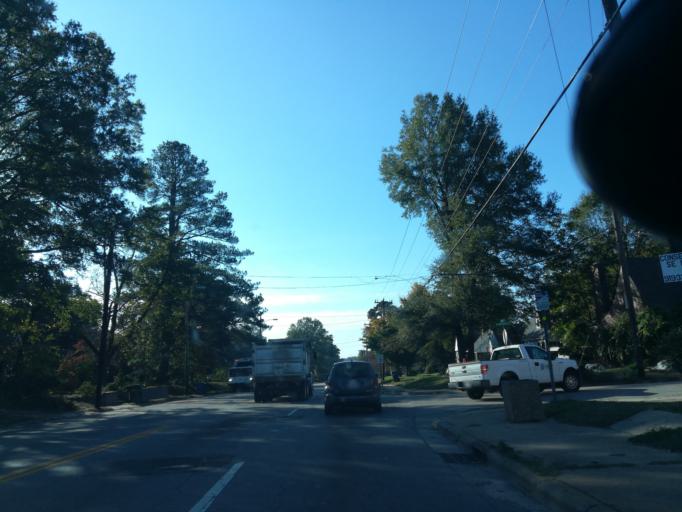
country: US
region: North Carolina
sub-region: Durham County
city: Durham
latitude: 36.0268
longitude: -78.8898
